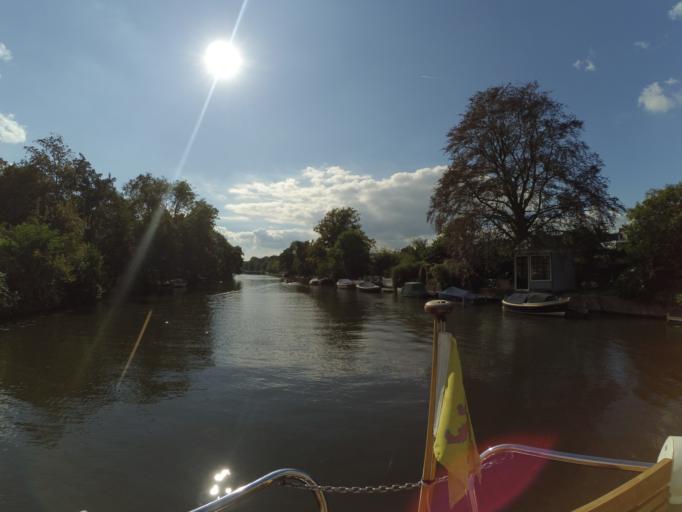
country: NL
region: Utrecht
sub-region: Stichtse Vecht
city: Vreeland
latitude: 52.2081
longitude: 5.0225
